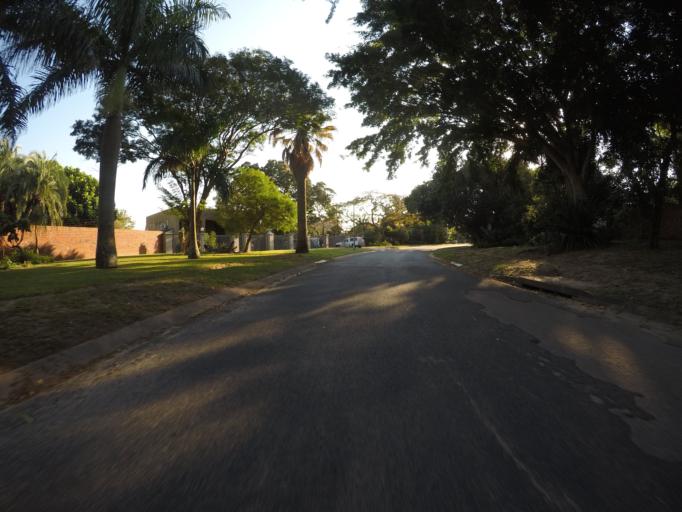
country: ZA
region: KwaZulu-Natal
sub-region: uThungulu District Municipality
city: Richards Bay
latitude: -28.7737
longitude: 32.1038
